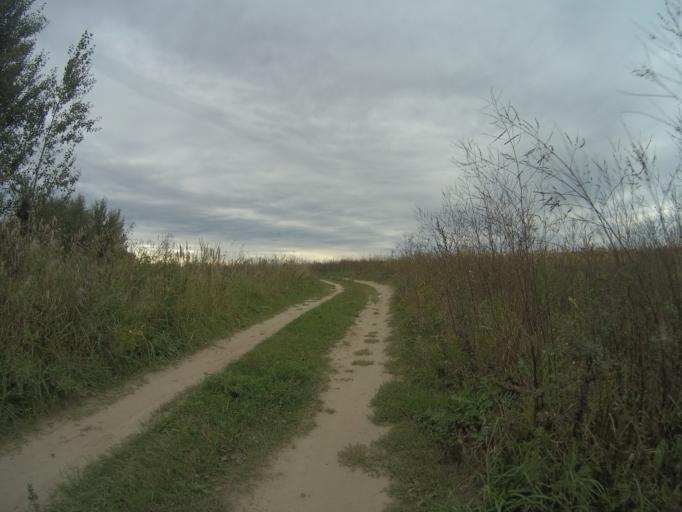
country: RU
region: Vladimir
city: Golovino
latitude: 55.9773
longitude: 40.4851
